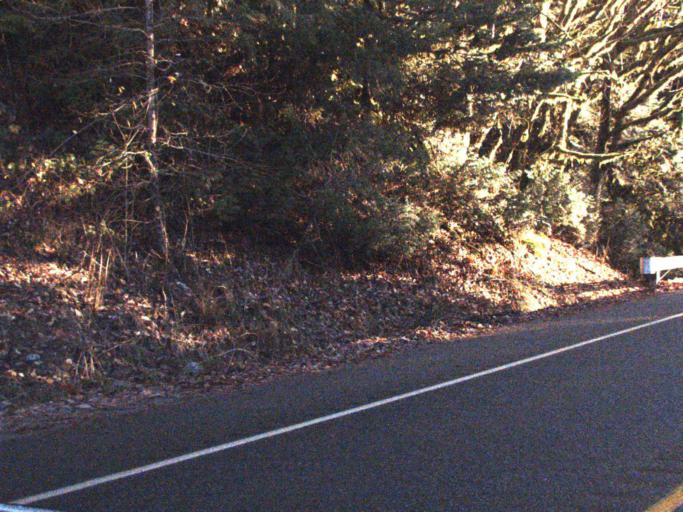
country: US
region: Washington
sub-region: Snohomish County
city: Darrington
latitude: 48.4879
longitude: -121.6004
